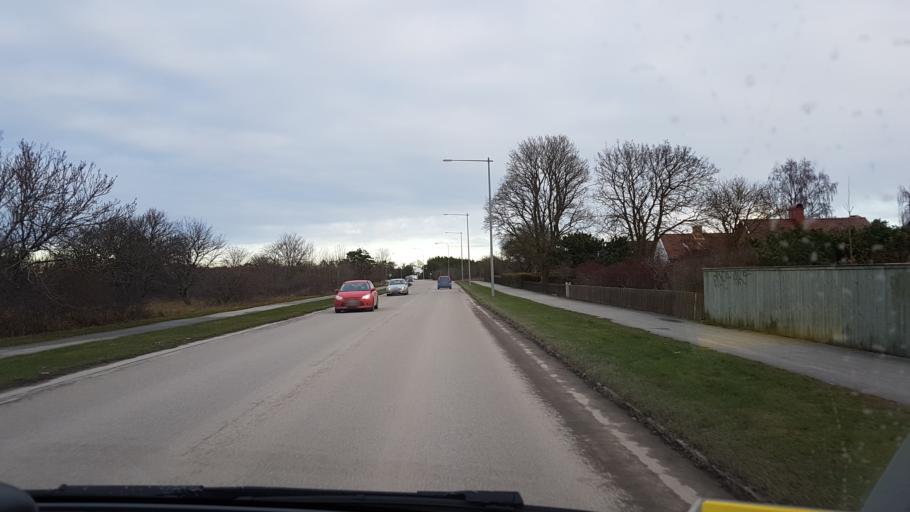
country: SE
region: Gotland
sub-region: Gotland
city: Visby
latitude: 57.6495
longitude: 18.3146
